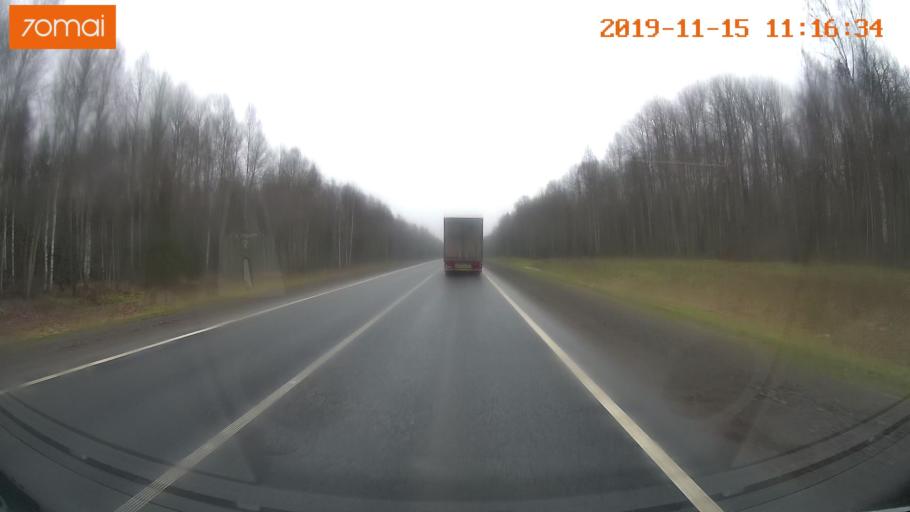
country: RU
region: Vologda
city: Chebsara
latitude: 59.1307
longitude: 39.2328
